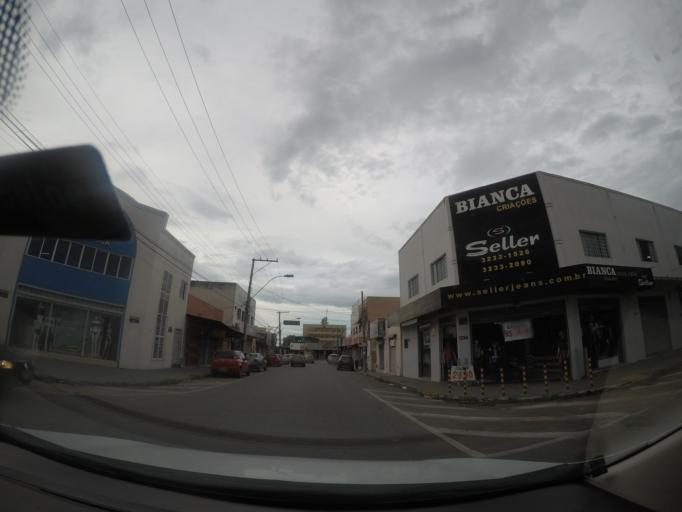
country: BR
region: Goias
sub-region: Goiania
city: Goiania
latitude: -16.6671
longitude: -49.2847
